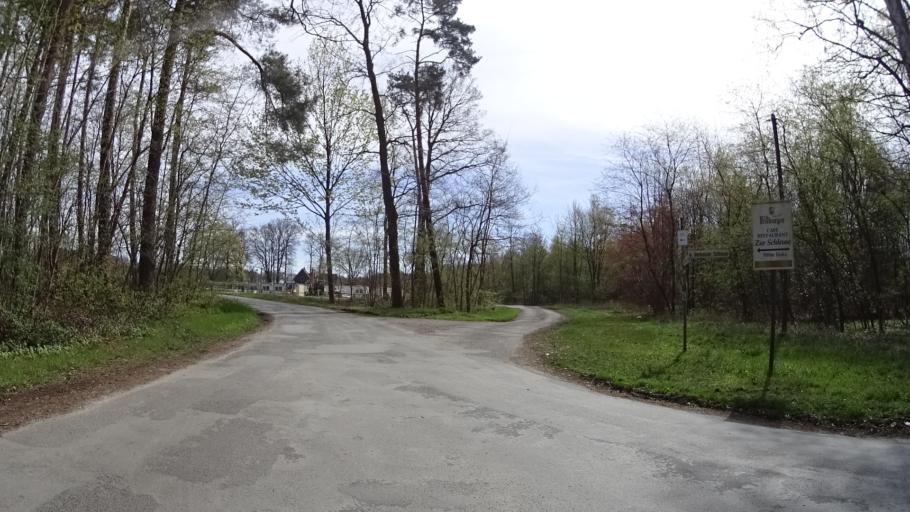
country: DE
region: Lower Saxony
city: Spelle
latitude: 52.3730
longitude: 7.4057
